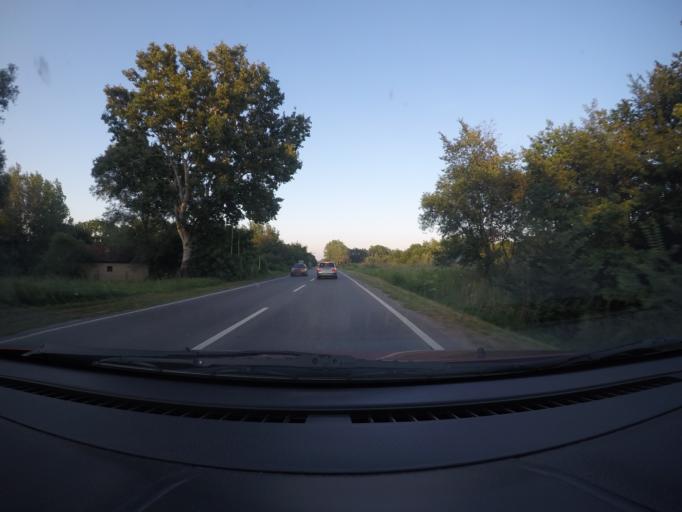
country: RS
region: Central Serbia
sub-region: Branicevski Okrug
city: Pozarevac
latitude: 44.6463
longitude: 21.2312
